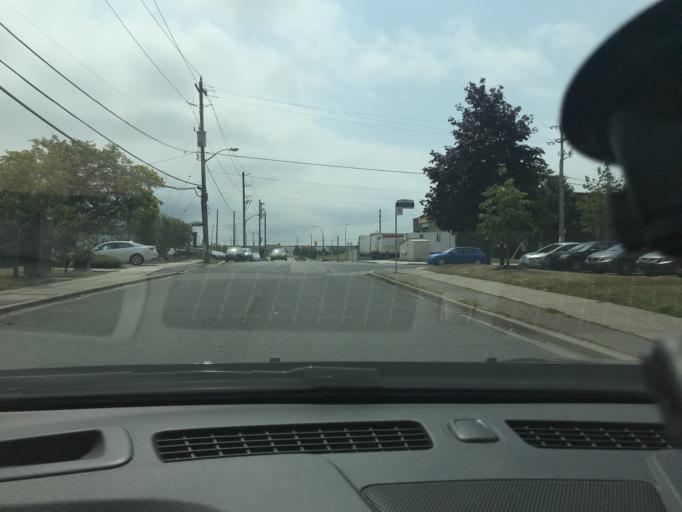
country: CA
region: Ontario
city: Concord
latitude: 43.7557
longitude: -79.4805
